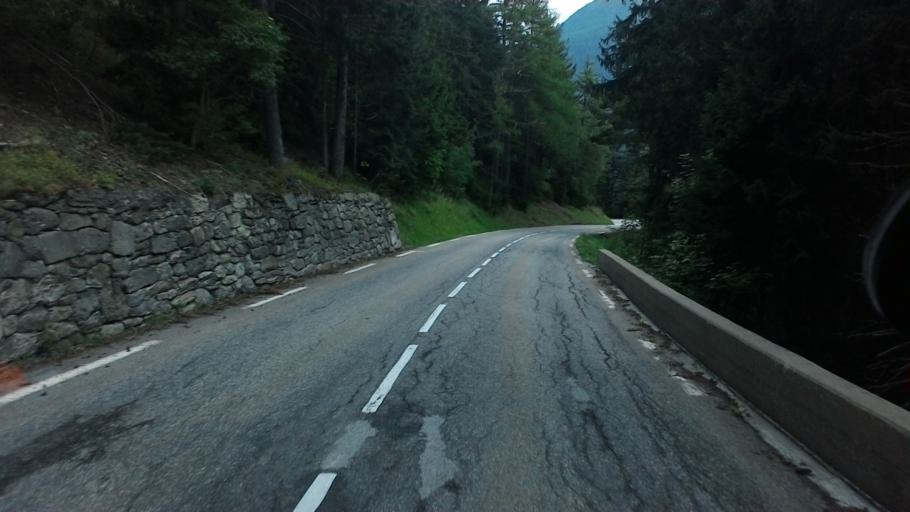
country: FR
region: Rhone-Alpes
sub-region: Departement de la Savoie
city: Seez
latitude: 45.6281
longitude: 6.8202
